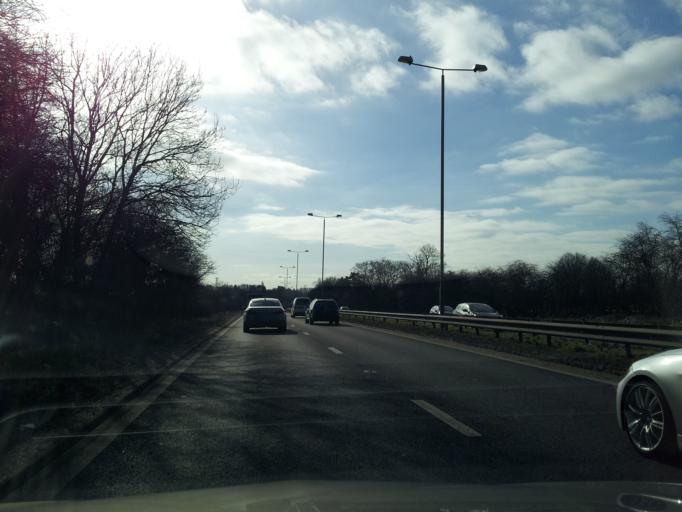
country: GB
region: England
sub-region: Derbyshire
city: Long Eaton
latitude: 52.9260
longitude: -1.2595
